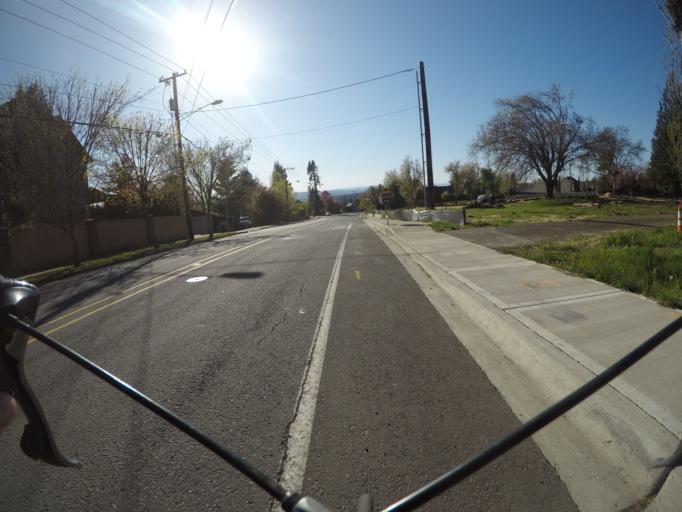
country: US
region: Oregon
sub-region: Washington County
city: King City
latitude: 45.4159
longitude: -122.8344
